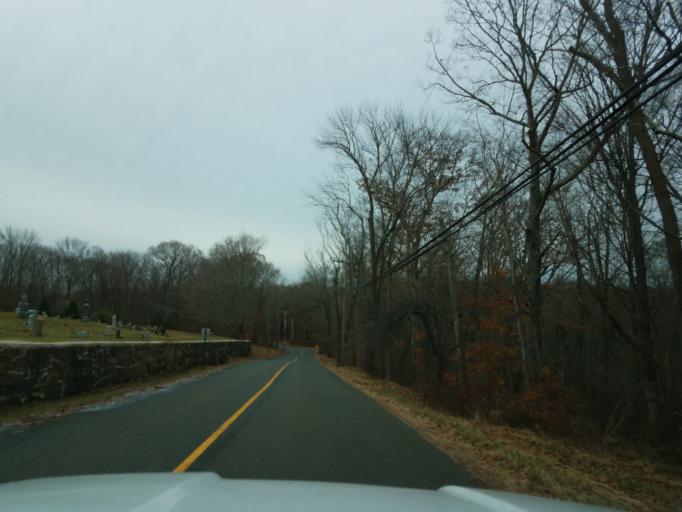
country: US
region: Connecticut
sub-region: New Haven County
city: North Branford
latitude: 41.3683
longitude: -72.7284
